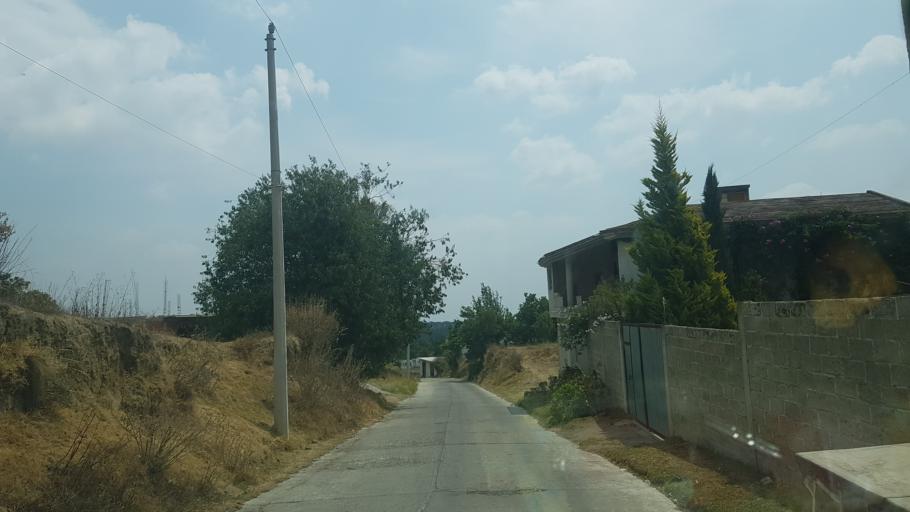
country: MX
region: Puebla
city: Domingo Arenas
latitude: 19.1376
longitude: -98.4805
